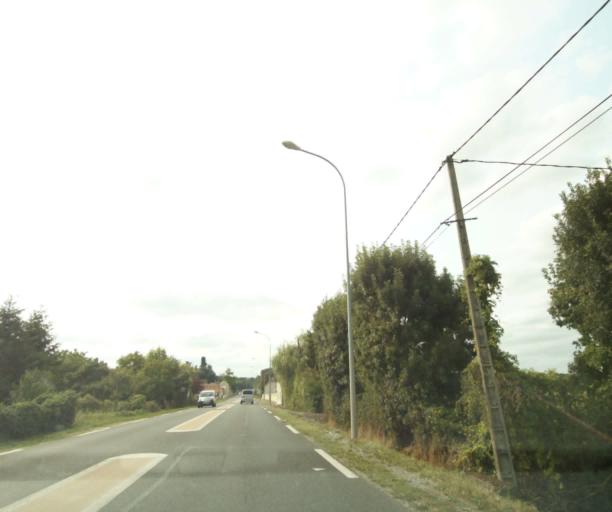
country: FR
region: Centre
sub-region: Departement de l'Indre
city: Clion
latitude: 46.9428
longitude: 1.2235
